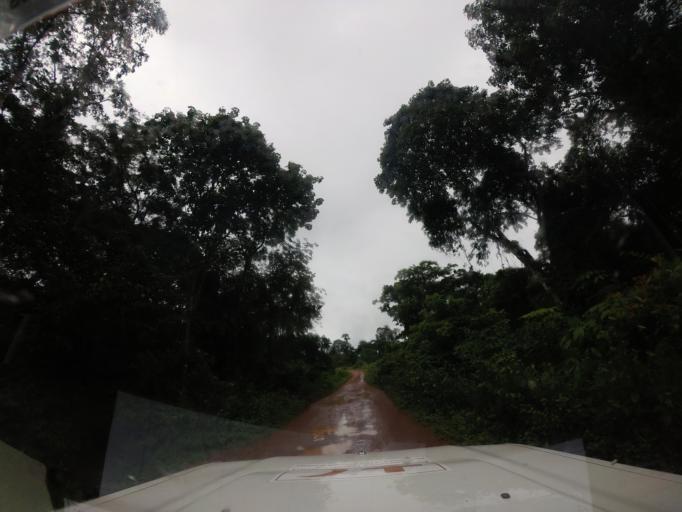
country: SL
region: Eastern Province
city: Kenema
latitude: 7.7177
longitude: -11.1900
